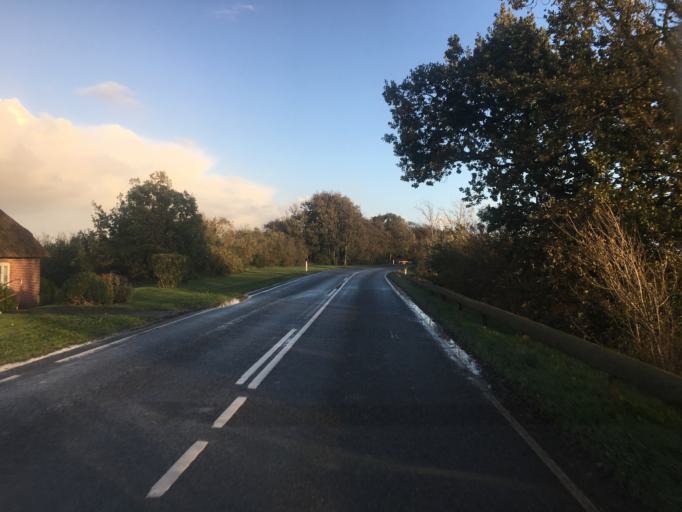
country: DE
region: Schleswig-Holstein
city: Neukirchen
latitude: 54.9146
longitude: 8.7391
